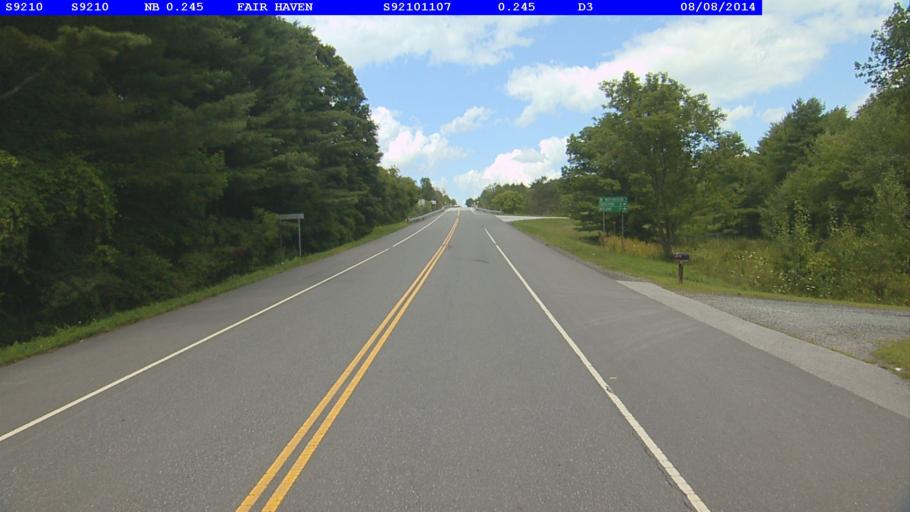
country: US
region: Vermont
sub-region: Rutland County
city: Fair Haven
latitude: 43.6030
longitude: -73.2608
